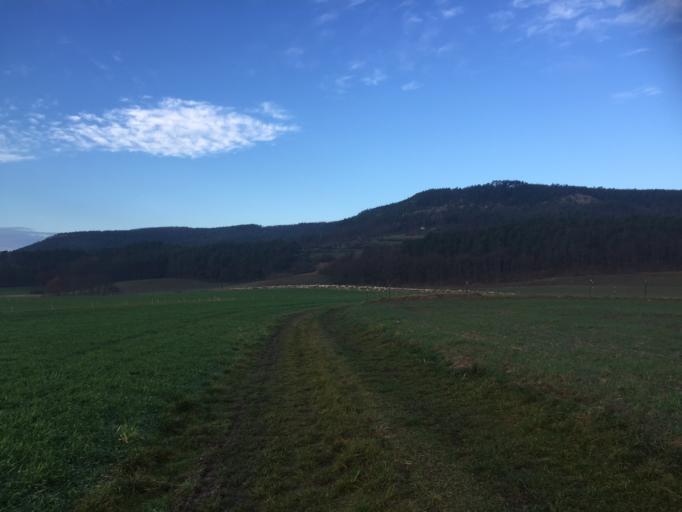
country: DE
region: Thuringia
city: Orlamunde
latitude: 50.7679
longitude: 11.4939
